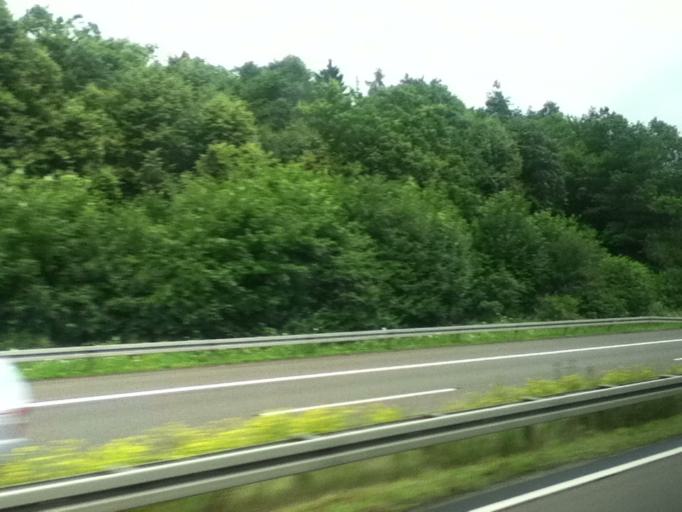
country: DE
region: Hesse
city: Kirtorf
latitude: 50.7151
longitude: 9.1348
